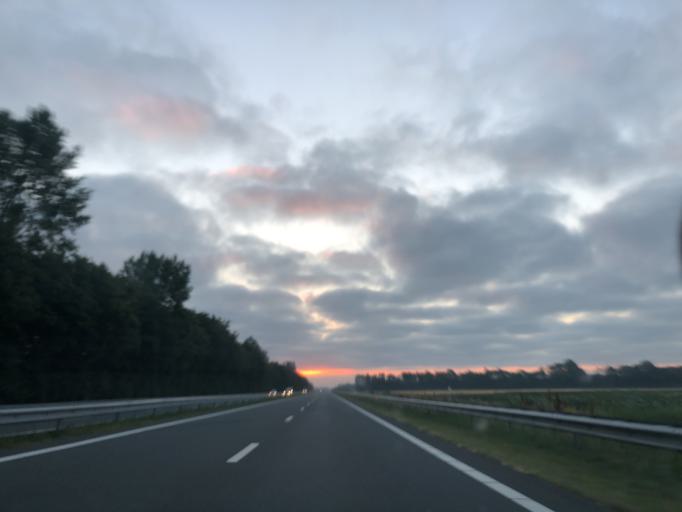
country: NL
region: Drenthe
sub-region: Gemeente Aa en Hunze
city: Anloo
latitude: 53.0257
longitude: 6.7859
